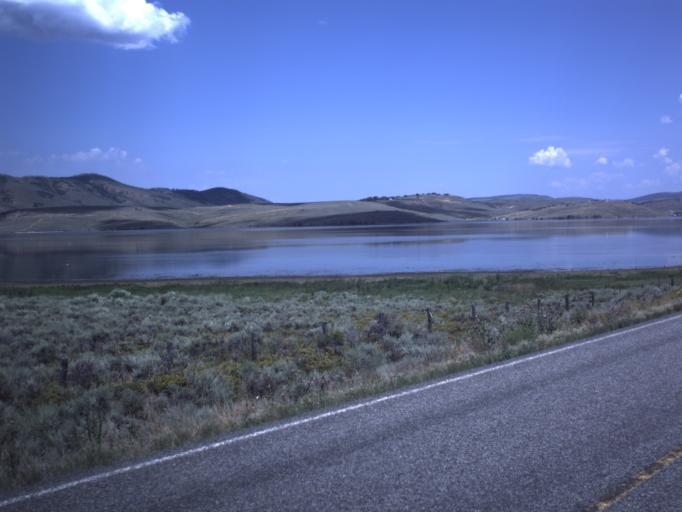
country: US
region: Utah
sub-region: Carbon County
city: Helper
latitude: 39.7639
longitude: -111.1423
